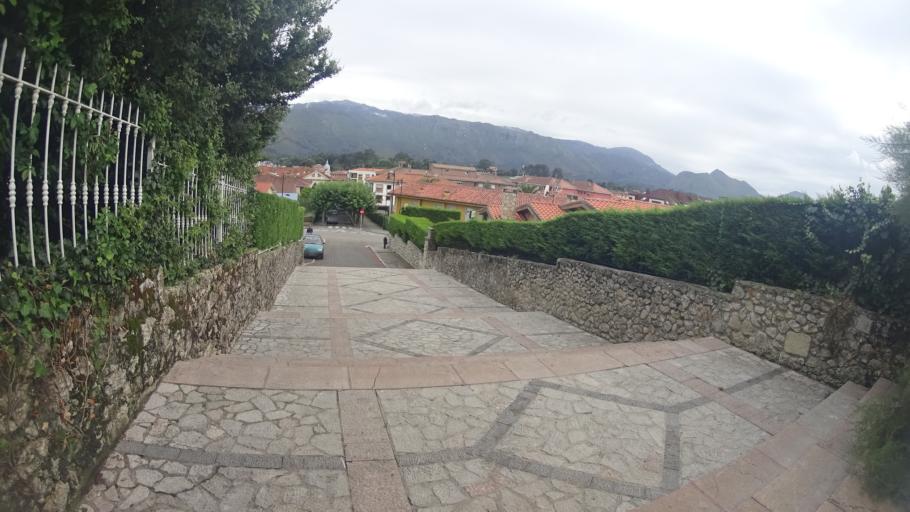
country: ES
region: Asturias
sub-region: Province of Asturias
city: Llanes
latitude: 43.4245
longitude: -4.7563
